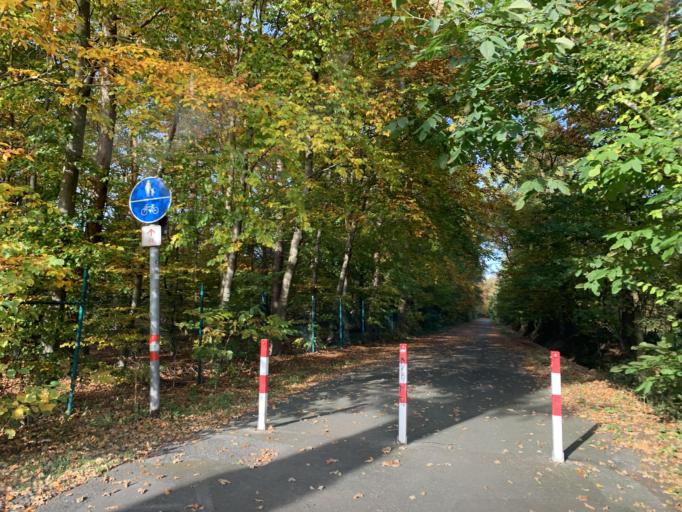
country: DE
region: North Rhine-Westphalia
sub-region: Regierungsbezirk Munster
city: Muenster
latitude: 51.9978
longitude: 7.6539
